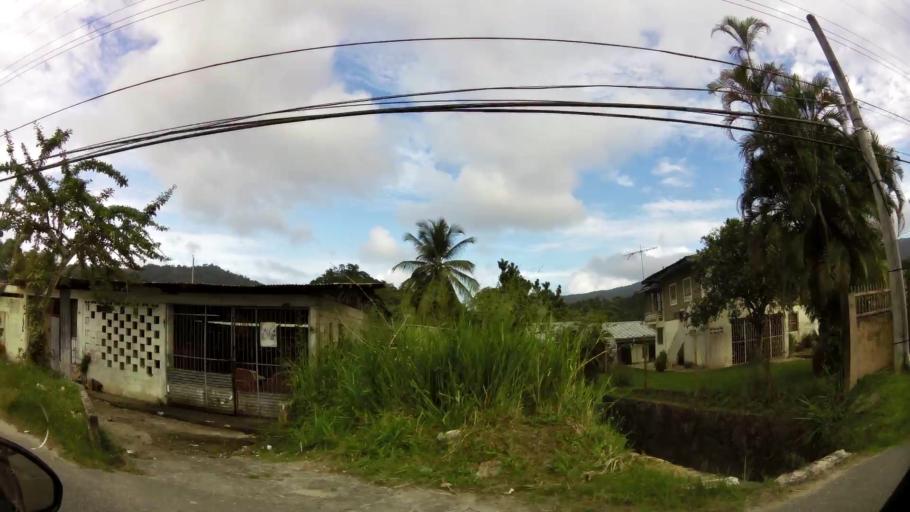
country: TT
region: Diego Martin
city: Petit Valley
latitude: 10.7138
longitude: -61.4767
